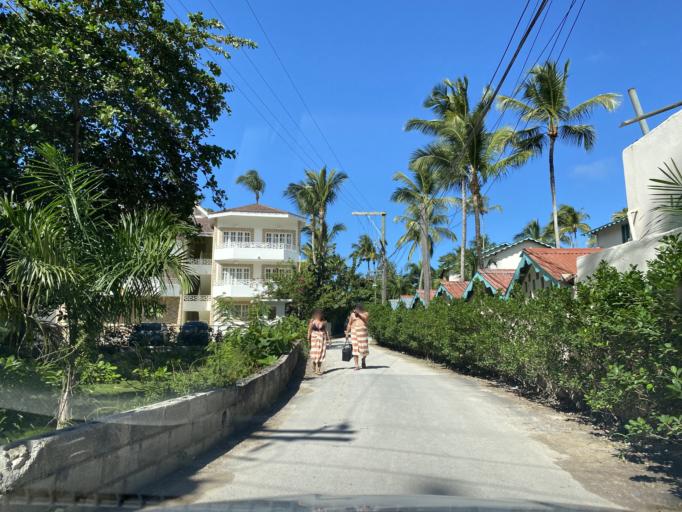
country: DO
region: Samana
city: Las Terrenas
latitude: 19.3244
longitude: -69.5515
